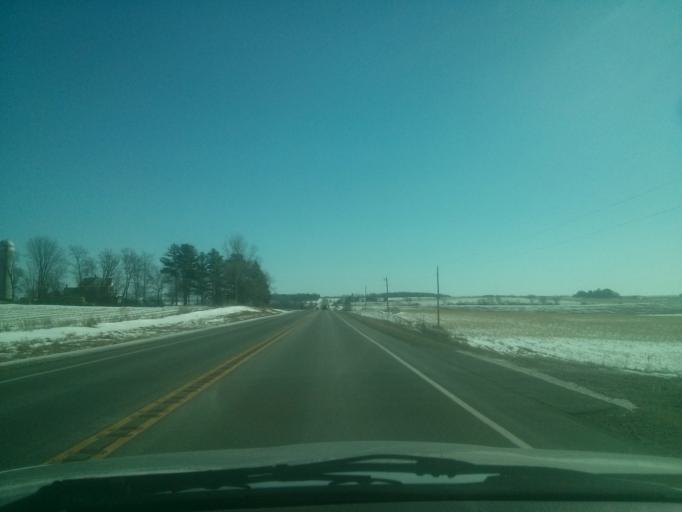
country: US
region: Wisconsin
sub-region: Polk County
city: Clear Lake
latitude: 45.1364
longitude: -92.3381
